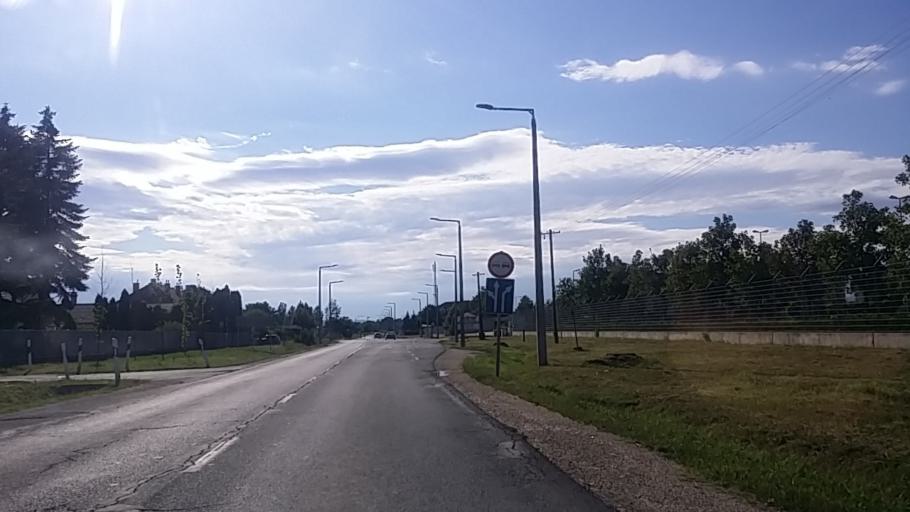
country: HU
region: Pest
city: Vac
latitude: 47.7728
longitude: 19.1553
